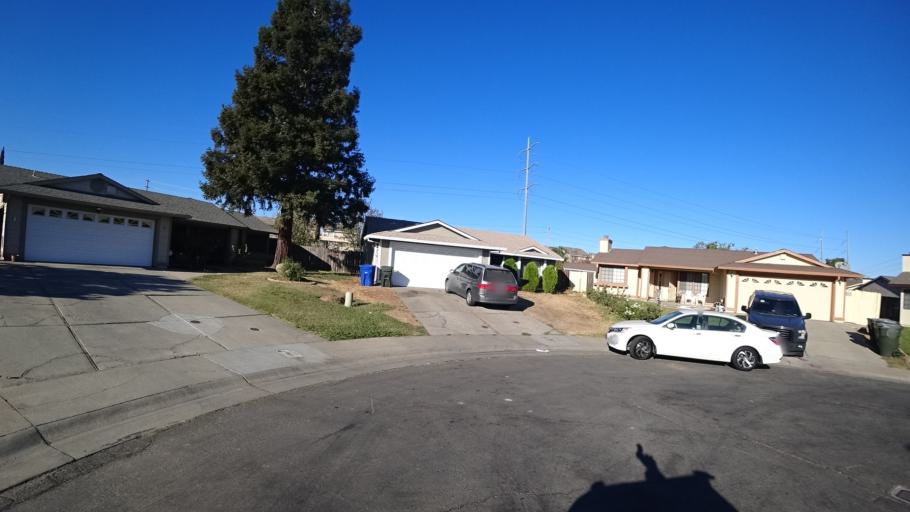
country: US
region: California
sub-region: Sacramento County
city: Parkway
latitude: 38.4876
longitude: -121.4674
